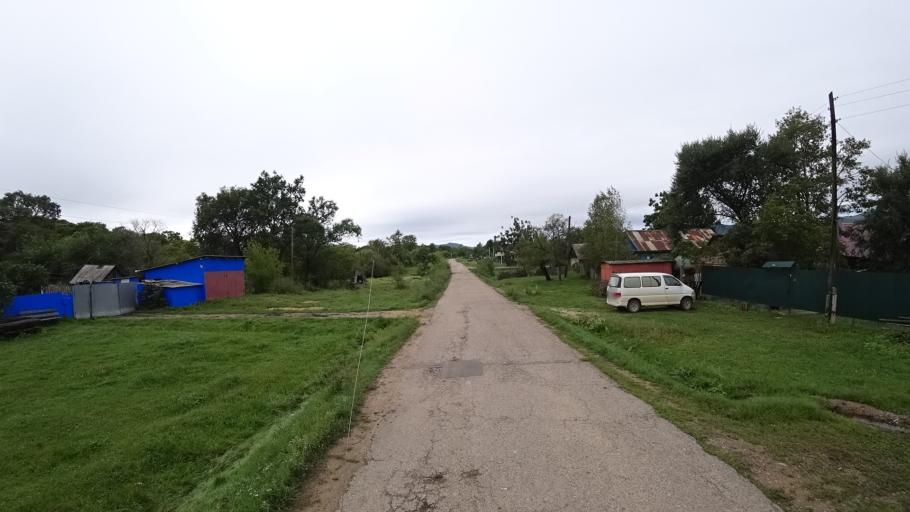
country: RU
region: Primorskiy
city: Monastyrishche
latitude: 44.0838
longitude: 132.5869
